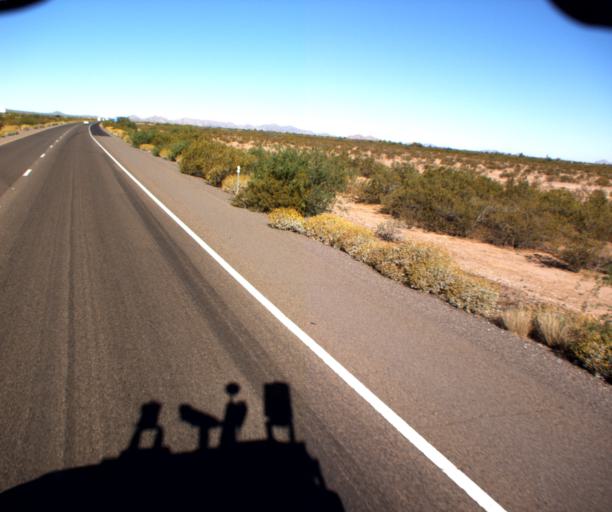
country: US
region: Arizona
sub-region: Pinal County
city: Casa Grande
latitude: 32.8284
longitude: -111.9678
